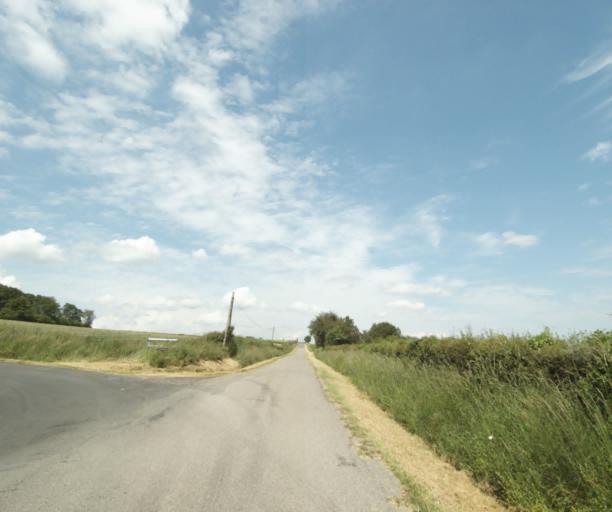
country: FR
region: Bourgogne
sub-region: Departement de Saone-et-Loire
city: Perrecy-les-Forges
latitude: 46.5900
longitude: 4.1408
